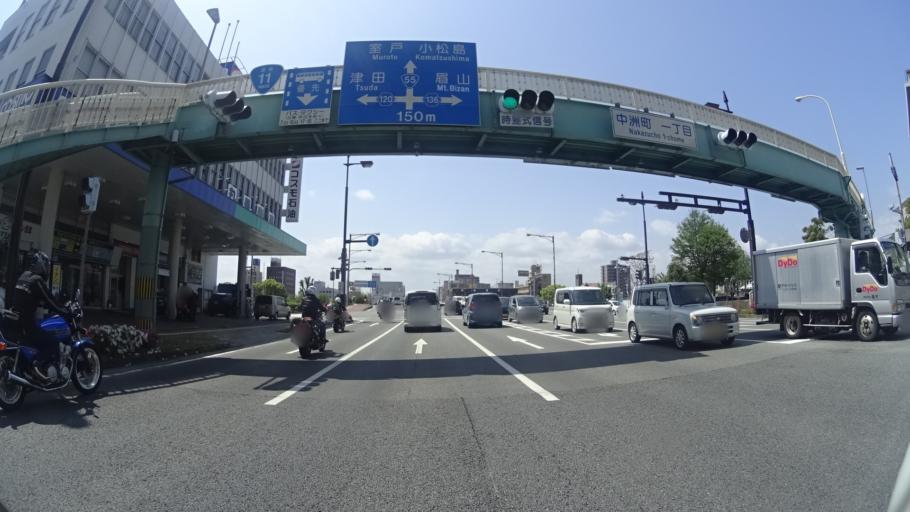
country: JP
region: Tokushima
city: Tokushima-shi
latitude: 34.0680
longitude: 134.5575
